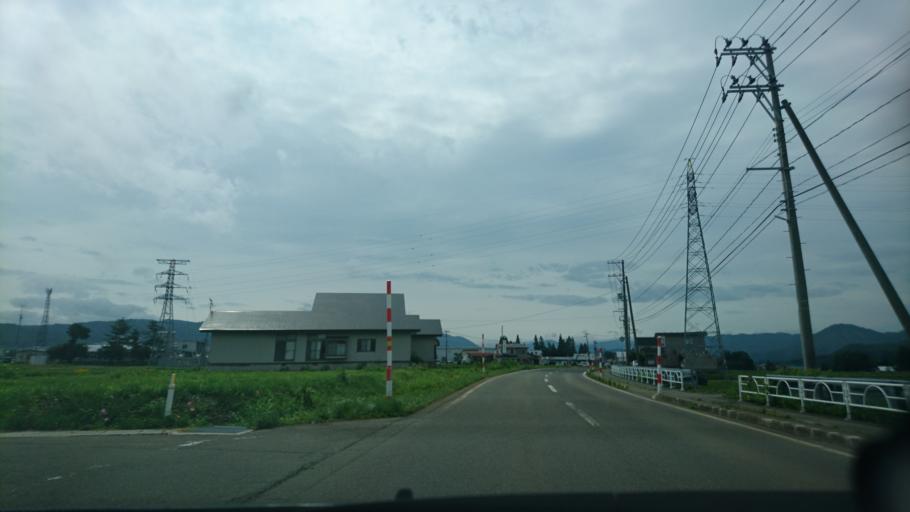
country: JP
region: Akita
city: Yuzawa
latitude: 39.1823
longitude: 140.5542
